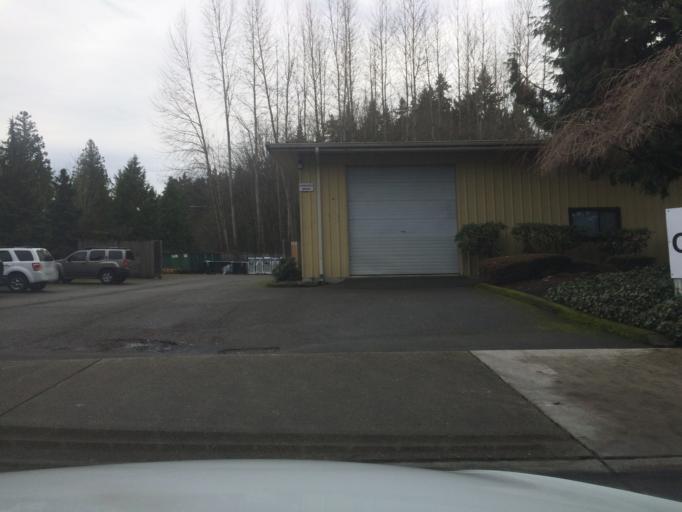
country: US
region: Washington
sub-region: King County
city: Redmond
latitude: 47.6805
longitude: -122.1458
